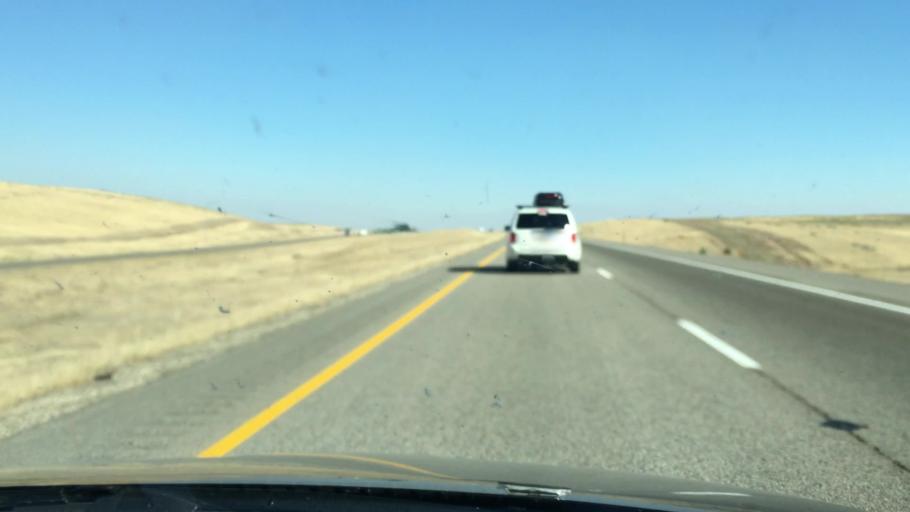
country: US
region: Idaho
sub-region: Ada County
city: Boise
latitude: 43.4873
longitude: -116.1213
